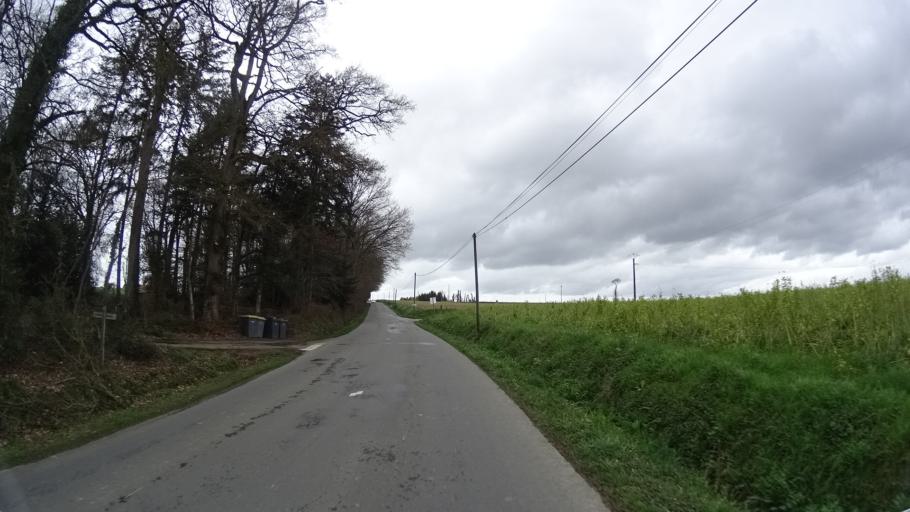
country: FR
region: Brittany
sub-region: Departement d'Ille-et-Vilaine
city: Saint-Gilles
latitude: 48.1809
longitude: -1.8315
